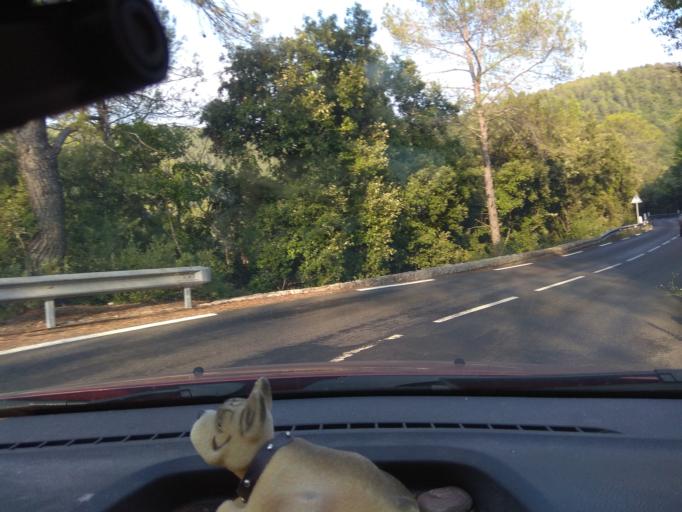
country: FR
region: Provence-Alpes-Cote d'Azur
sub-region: Departement des Alpes-Maritimes
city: Tourrettes-sur-Loup
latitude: 43.6882
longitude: 7.0679
